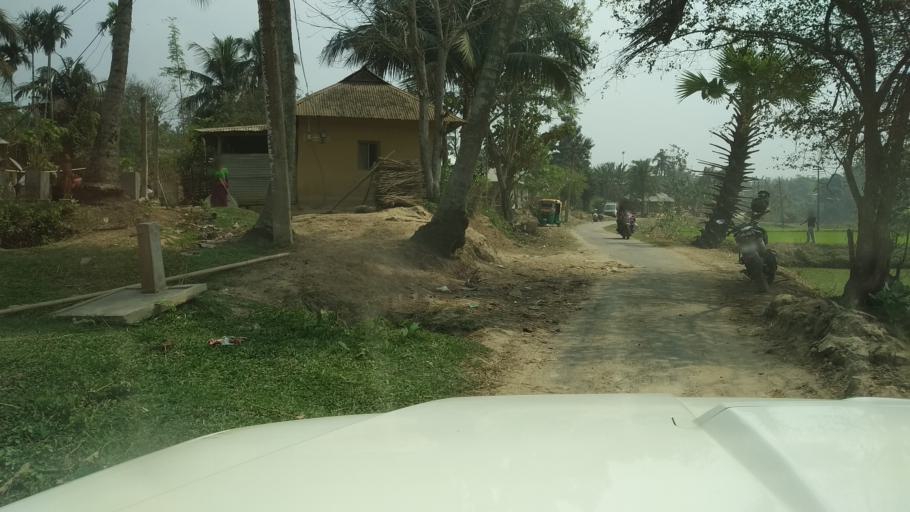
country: IN
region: Tripura
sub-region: West Tripura
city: Sonamura
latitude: 23.4282
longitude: 91.3201
